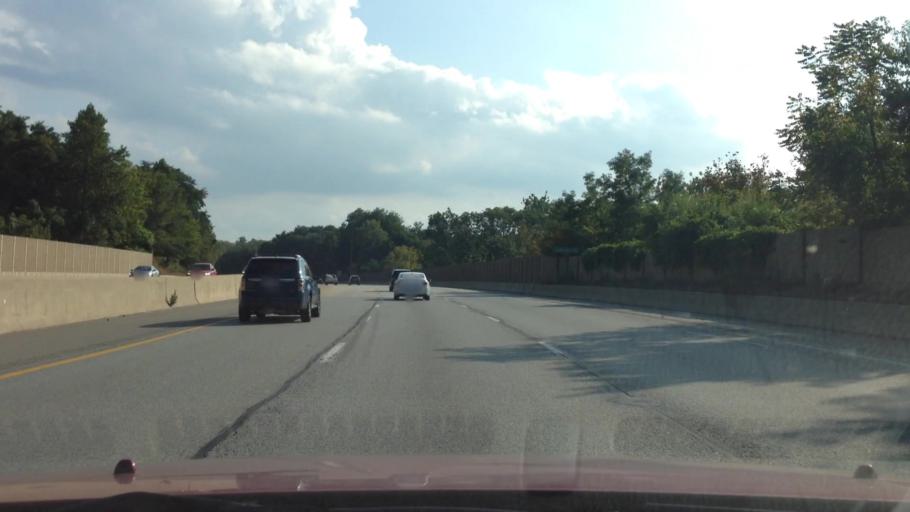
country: US
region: Pennsylvania
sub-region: Delaware County
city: Radnor
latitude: 40.0312
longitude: -75.3628
